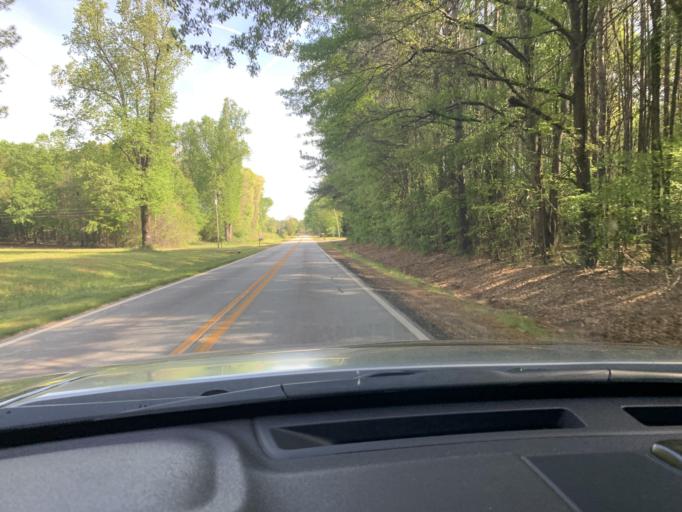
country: US
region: Georgia
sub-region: Oconee County
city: Watkinsville
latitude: 33.7976
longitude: -83.3200
